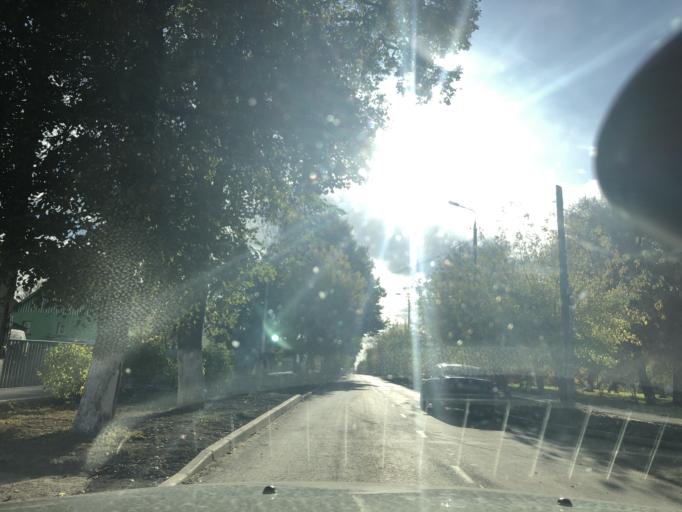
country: RU
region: Tula
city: Kireyevsk
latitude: 53.9369
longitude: 37.9320
